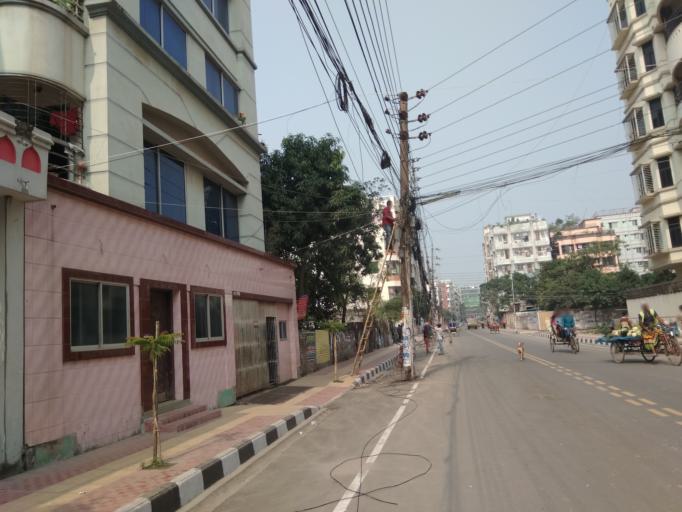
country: BD
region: Dhaka
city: Tungi
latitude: 23.8657
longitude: 90.3857
